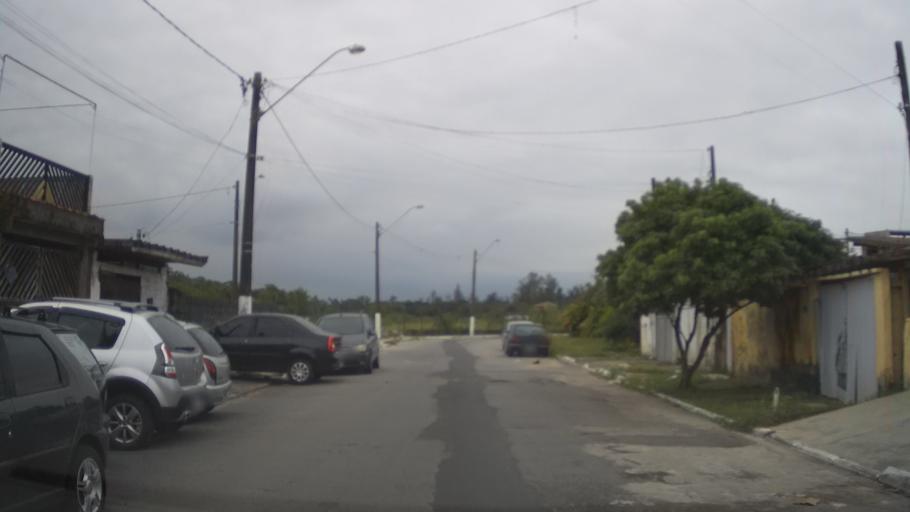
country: BR
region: Sao Paulo
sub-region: Praia Grande
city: Praia Grande
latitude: -24.0064
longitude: -46.4597
